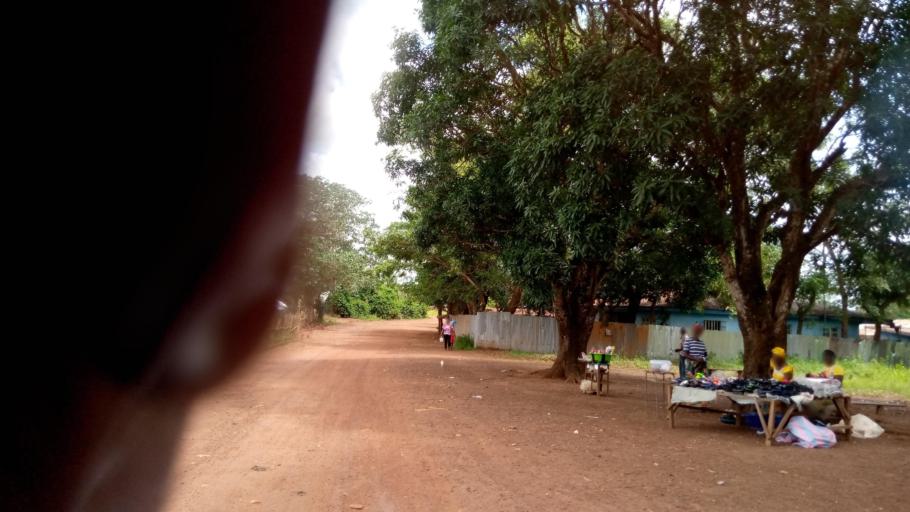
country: SL
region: Northern Province
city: Kamakwie
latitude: 9.4942
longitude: -12.2361
